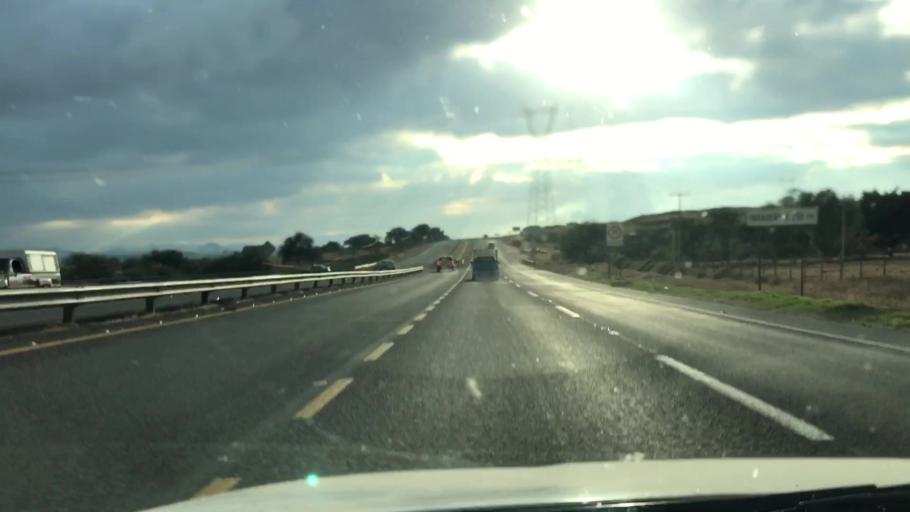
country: MX
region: Guanajuato
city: Penjamo
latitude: 20.4003
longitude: -101.7502
